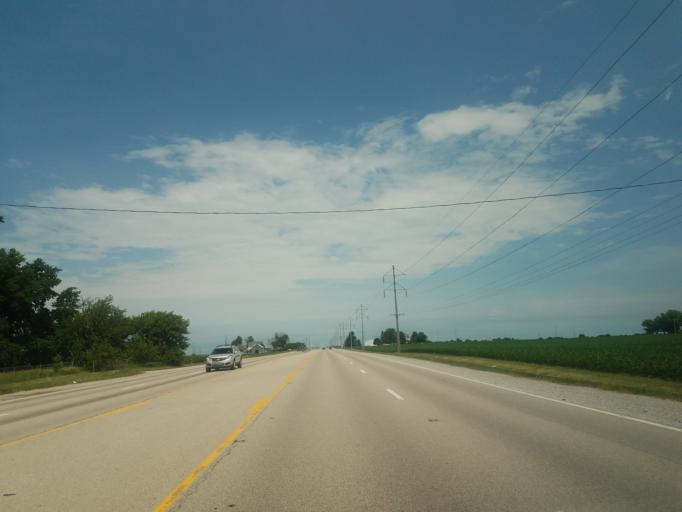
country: US
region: Illinois
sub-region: McLean County
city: Downs
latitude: 40.4389
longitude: -88.9016
